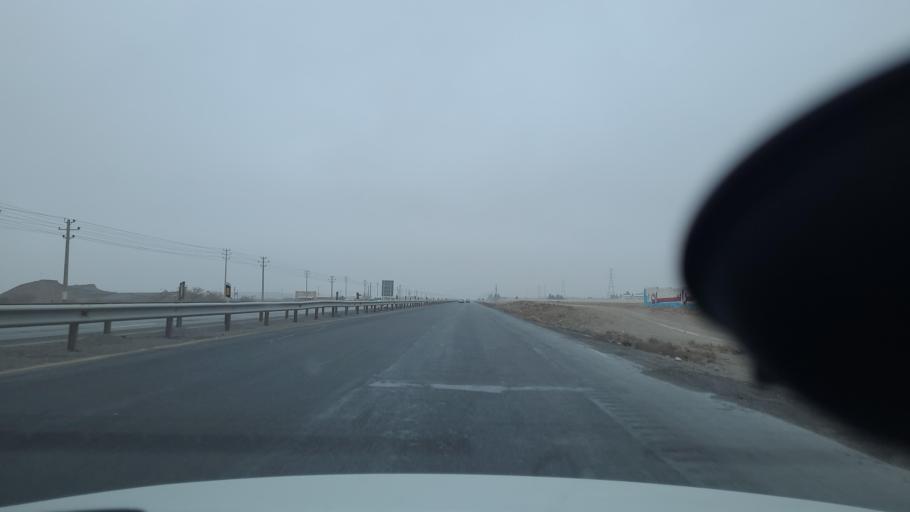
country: IR
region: Razavi Khorasan
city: Fariman
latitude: 35.9319
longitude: 59.7519
